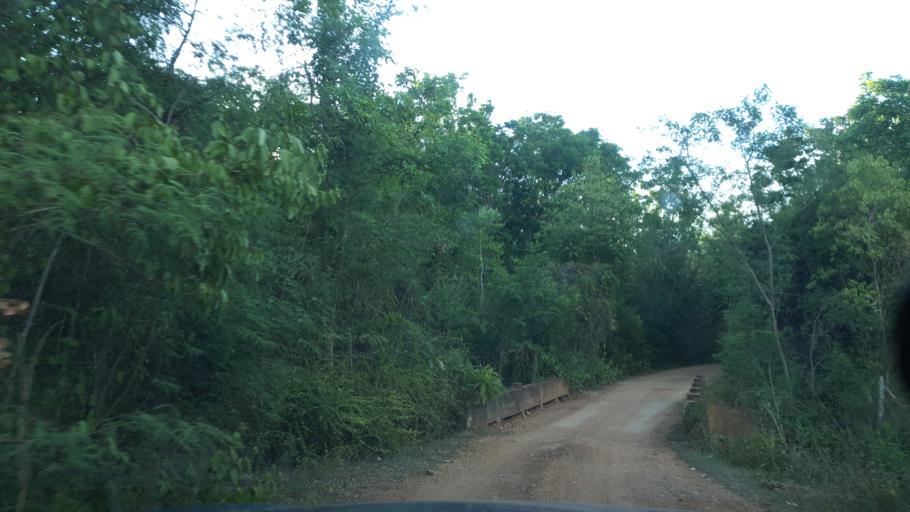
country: TH
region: Lampang
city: Sop Prap
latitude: 17.9532
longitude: 99.3487
